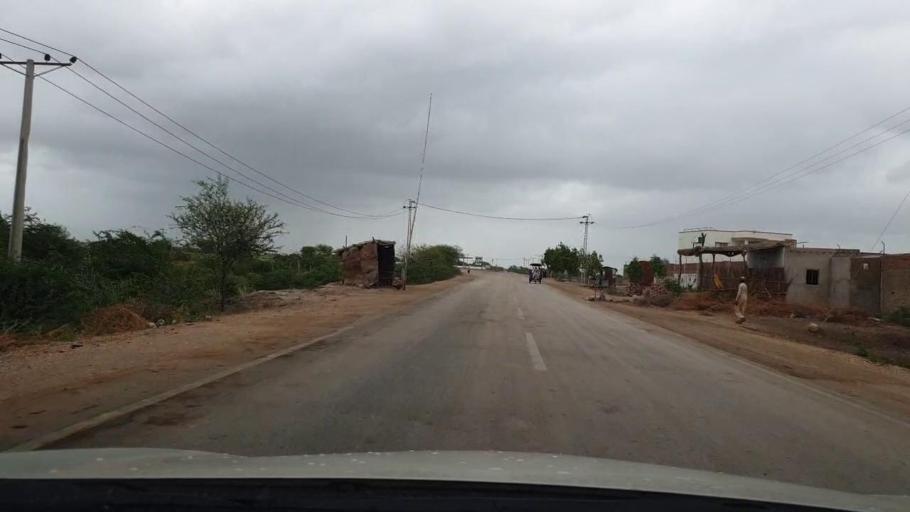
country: PK
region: Sindh
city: Badin
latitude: 24.6524
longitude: 68.7726
